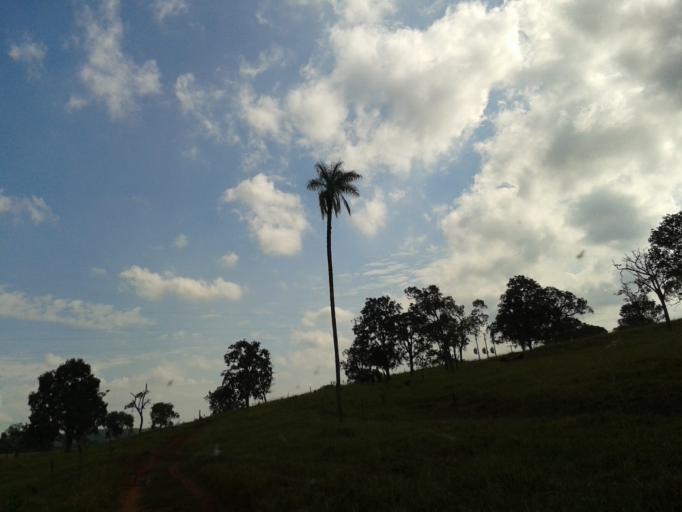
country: BR
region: Minas Gerais
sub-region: Campina Verde
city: Campina Verde
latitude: -19.3934
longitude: -49.6865
